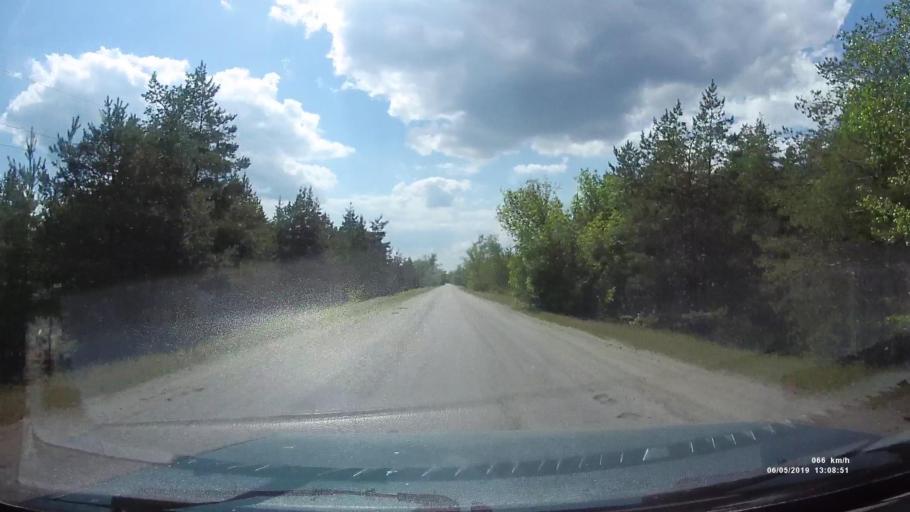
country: RU
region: Rostov
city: Ust'-Donetskiy
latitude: 47.7728
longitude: 40.9909
